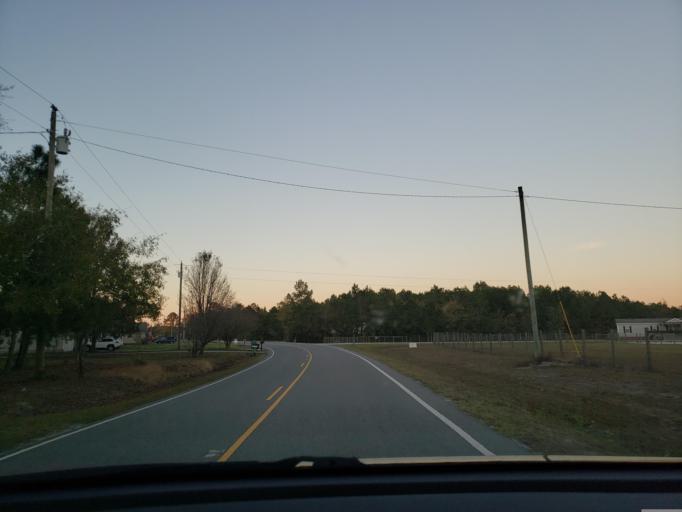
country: US
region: North Carolina
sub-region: Onslow County
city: Richlands
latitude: 34.7324
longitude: -77.6229
